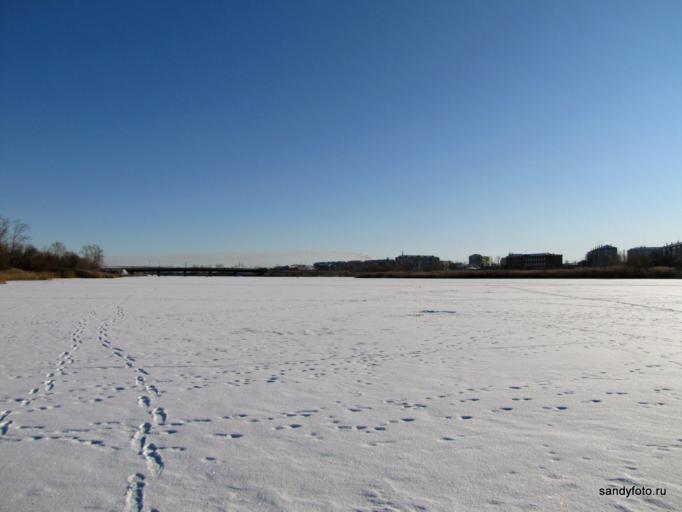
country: RU
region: Chelyabinsk
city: Troitsk
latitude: 54.0948
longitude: 61.5602
